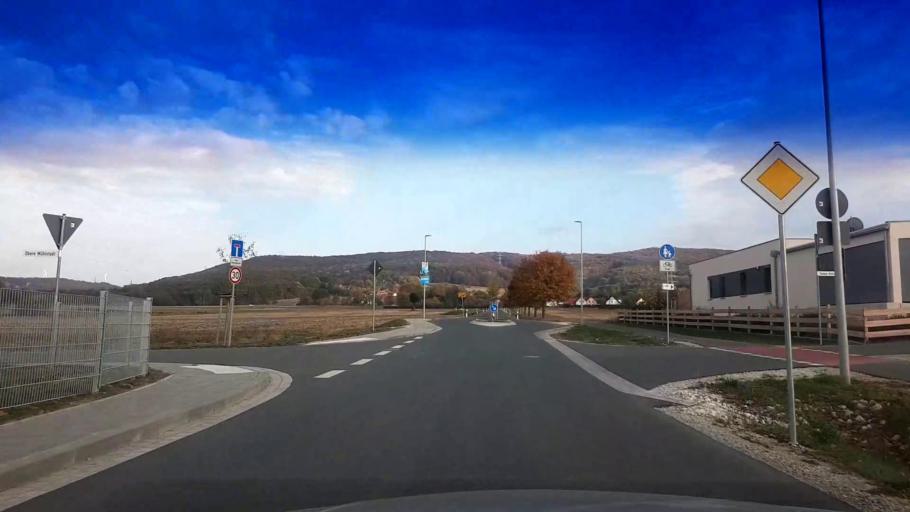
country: DE
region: Bavaria
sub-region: Upper Franconia
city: Schesslitz
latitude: 49.9735
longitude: 11.0482
